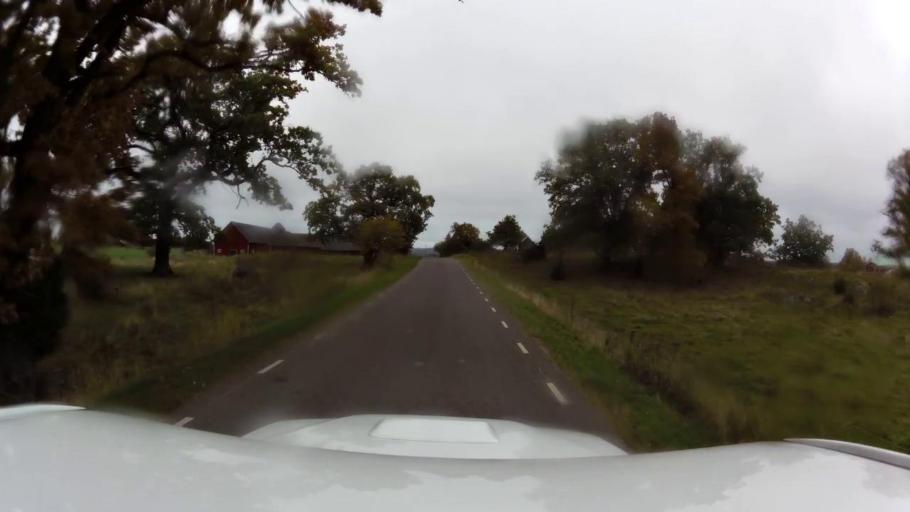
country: SE
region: OEstergoetland
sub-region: Linkopings Kommun
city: Linghem
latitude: 58.4780
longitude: 15.7580
